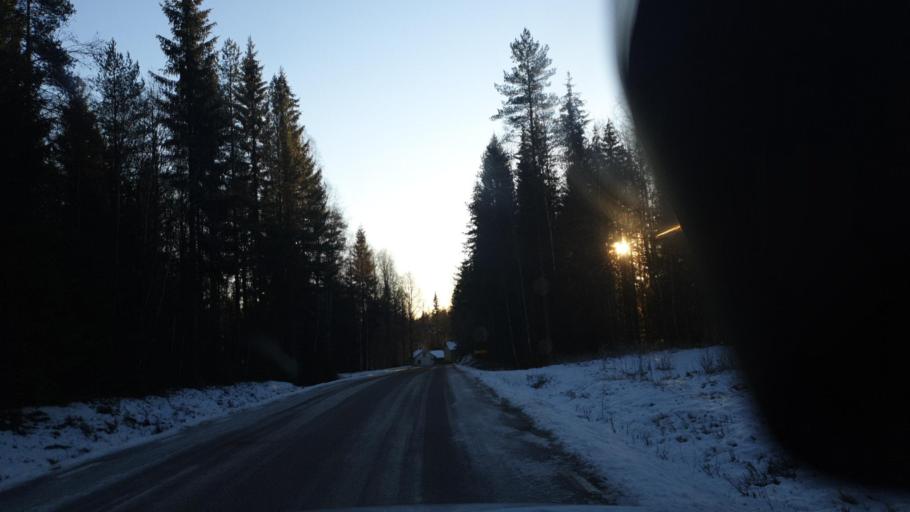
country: SE
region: Vaermland
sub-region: Arvika Kommun
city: Arvika
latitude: 59.7976
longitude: 12.8379
